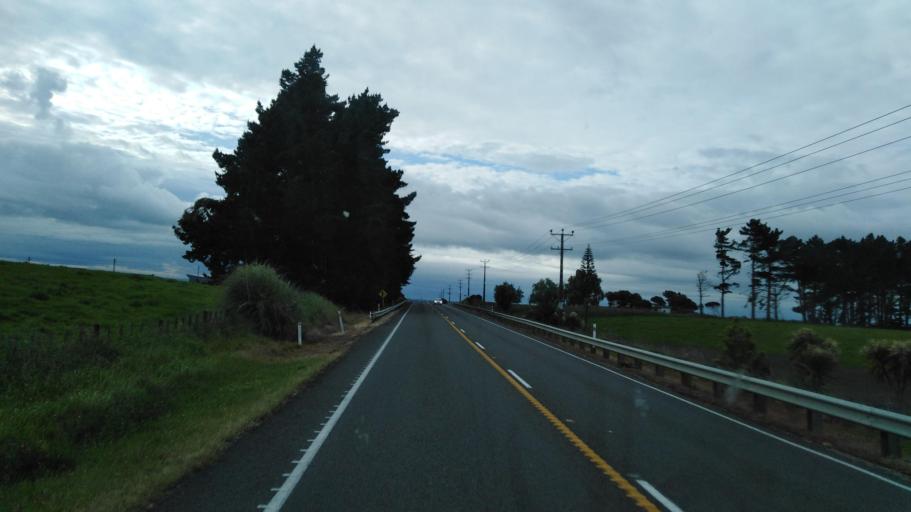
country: NZ
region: Manawatu-Wanganui
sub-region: Rangitikei District
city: Bulls
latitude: -40.1396
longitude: 175.3663
